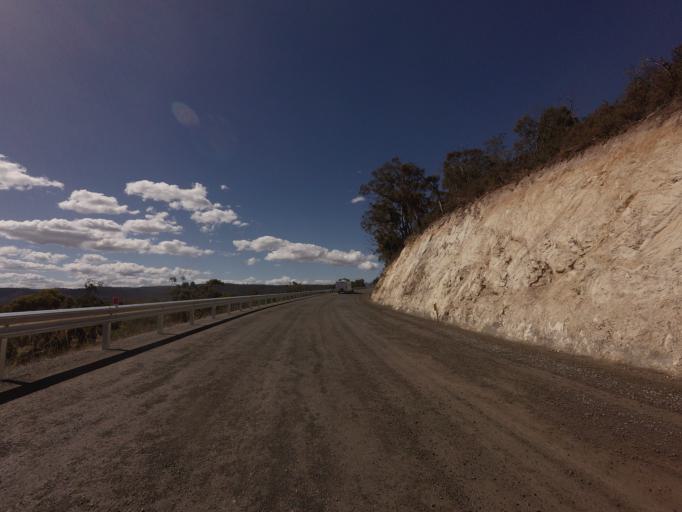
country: AU
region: Tasmania
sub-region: Break O'Day
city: St Helens
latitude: -41.6583
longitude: 147.9156
